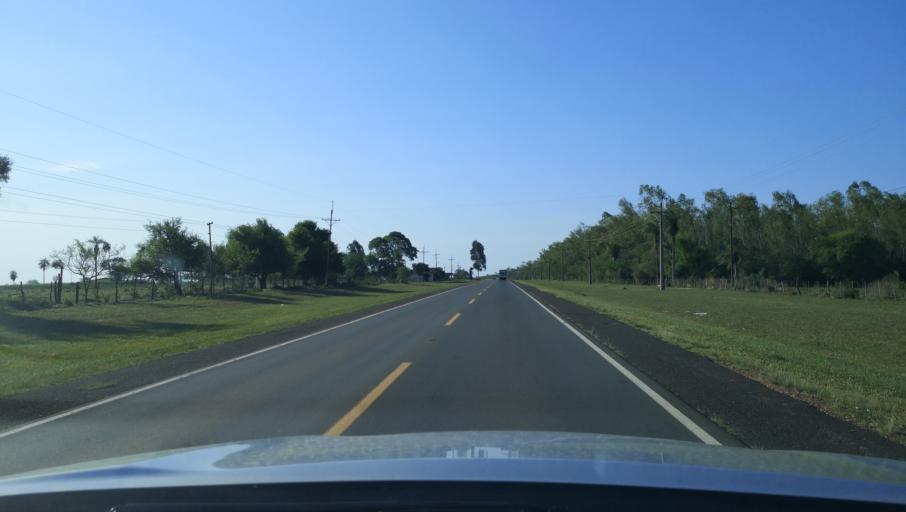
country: PY
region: Misiones
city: Santa Maria
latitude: -26.7666
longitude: -57.0320
